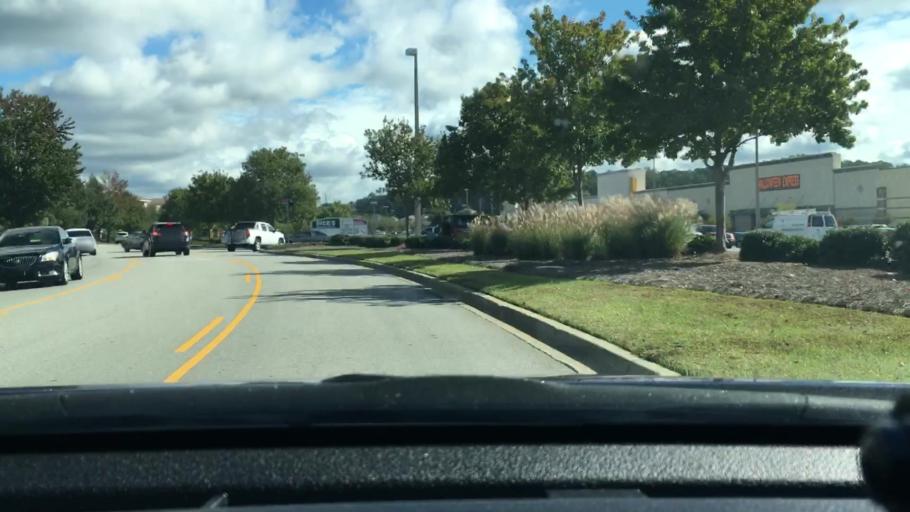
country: US
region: South Carolina
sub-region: Lexington County
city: Seven Oaks
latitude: 34.0687
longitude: -81.1601
